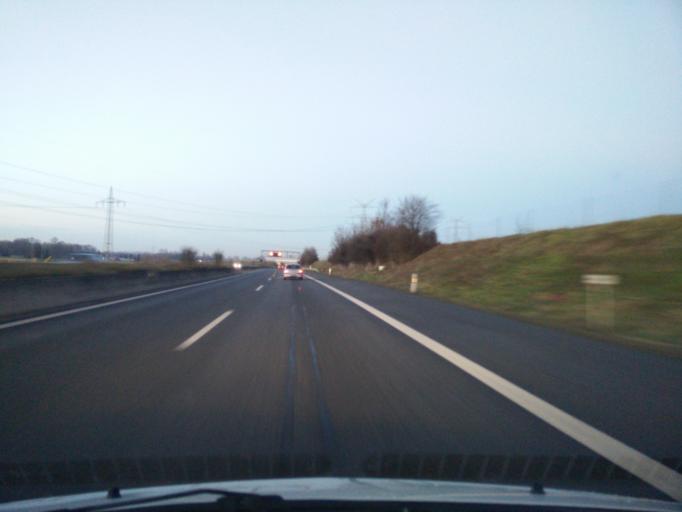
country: DE
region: Bavaria
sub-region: Upper Bavaria
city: Karlsfeld
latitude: 48.1939
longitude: 11.4376
